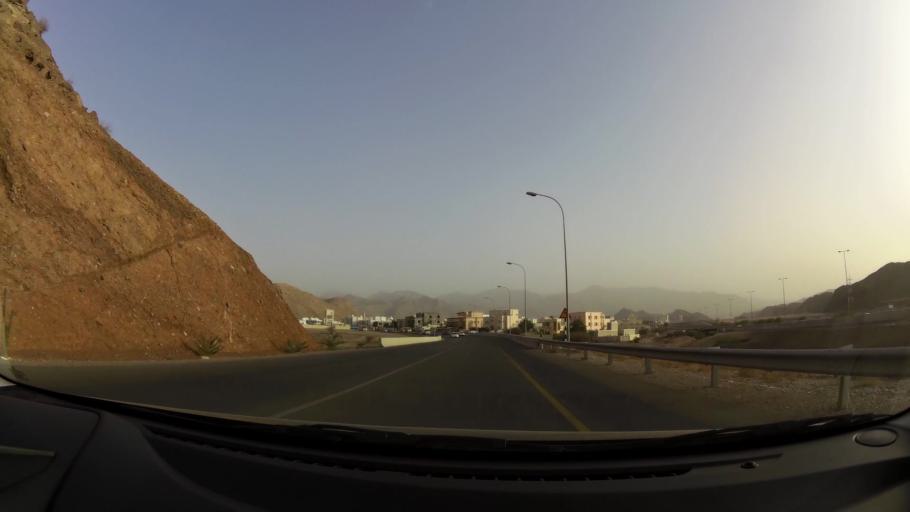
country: OM
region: Muhafazat Masqat
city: Bawshar
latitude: 23.5156
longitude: 58.3460
